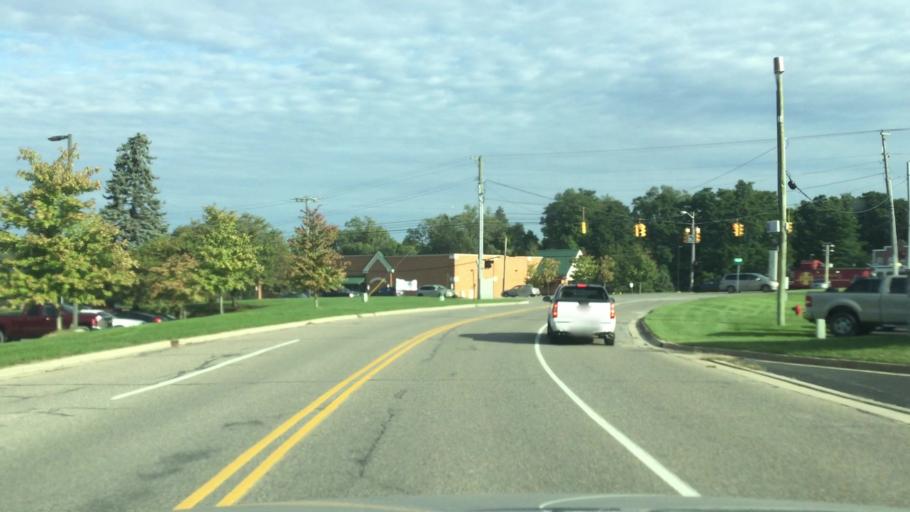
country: US
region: Michigan
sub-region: Livingston County
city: Howell
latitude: 42.5977
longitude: -83.9063
